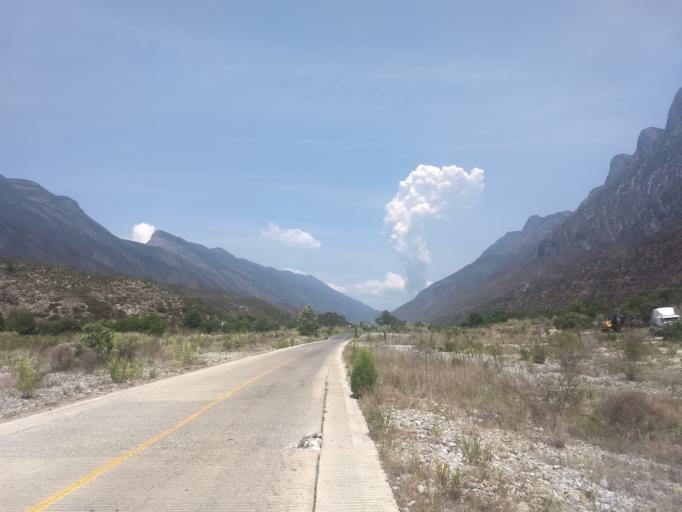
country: MX
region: Nuevo Leon
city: Santiago
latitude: 25.3954
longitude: -100.2919
